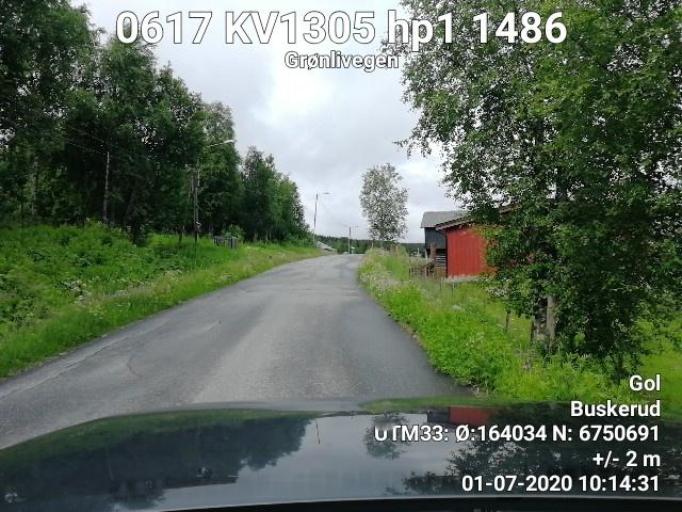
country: NO
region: Buskerud
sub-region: Gol
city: Gol
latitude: 60.7495
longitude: 8.8305
